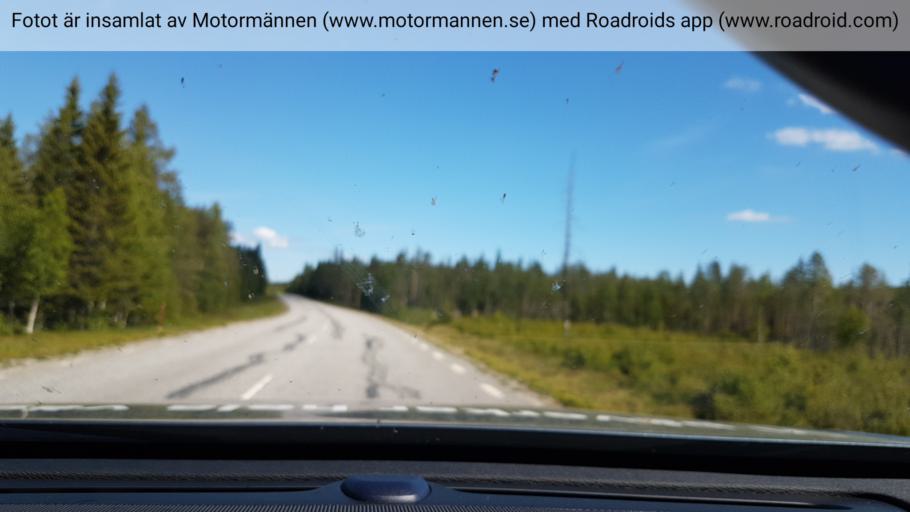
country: SE
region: Vaesterbotten
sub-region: Lycksele Kommun
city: Soderfors
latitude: 64.6235
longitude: 18.1054
